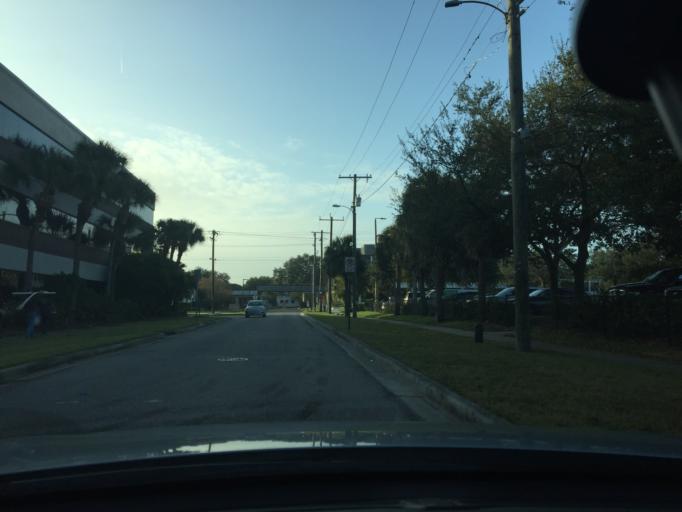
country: US
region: Florida
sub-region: Hillsborough County
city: Tampa
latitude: 27.9395
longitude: -82.4892
